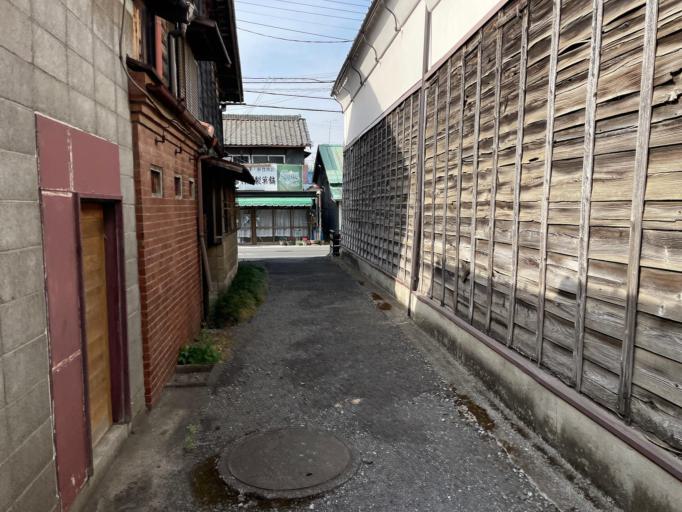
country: JP
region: Saitama
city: Fukayacho
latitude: 36.1947
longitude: 139.2750
